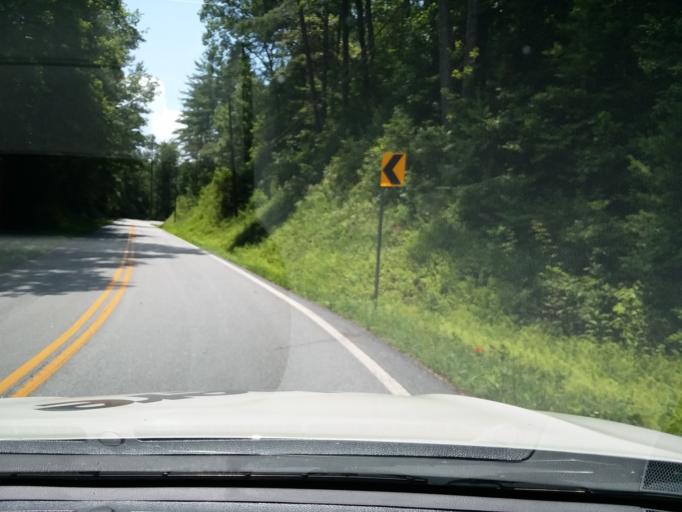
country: US
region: Georgia
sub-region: Rabun County
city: Mountain City
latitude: 34.9387
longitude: -83.1974
